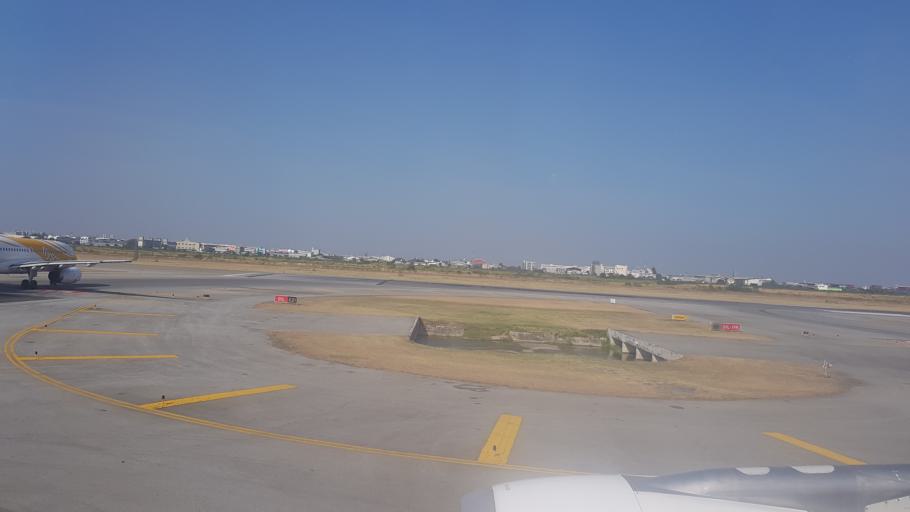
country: TH
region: Bangkok
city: Lat Krabang
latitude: 13.6713
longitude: 100.7365
